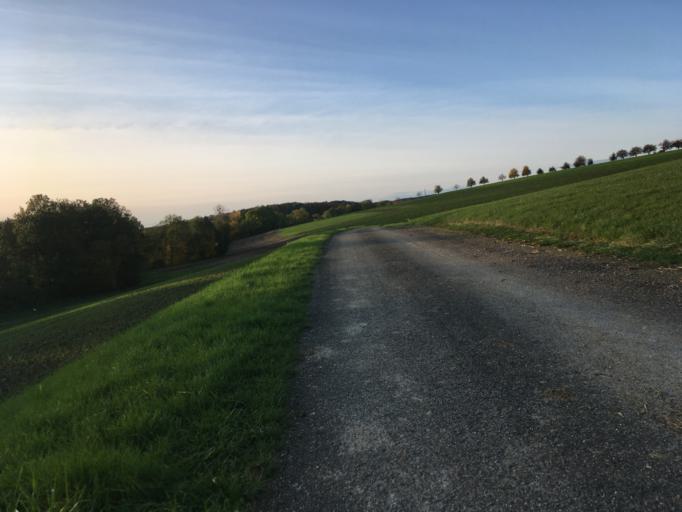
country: DE
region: Baden-Wuerttemberg
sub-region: Regierungsbezirk Stuttgart
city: Neuenstein
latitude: 49.2274
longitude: 9.5577
